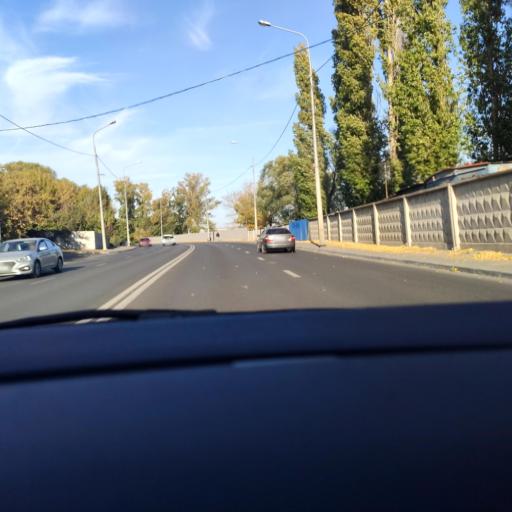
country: RU
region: Voronezj
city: Voronezh
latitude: 51.6870
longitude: 39.2303
